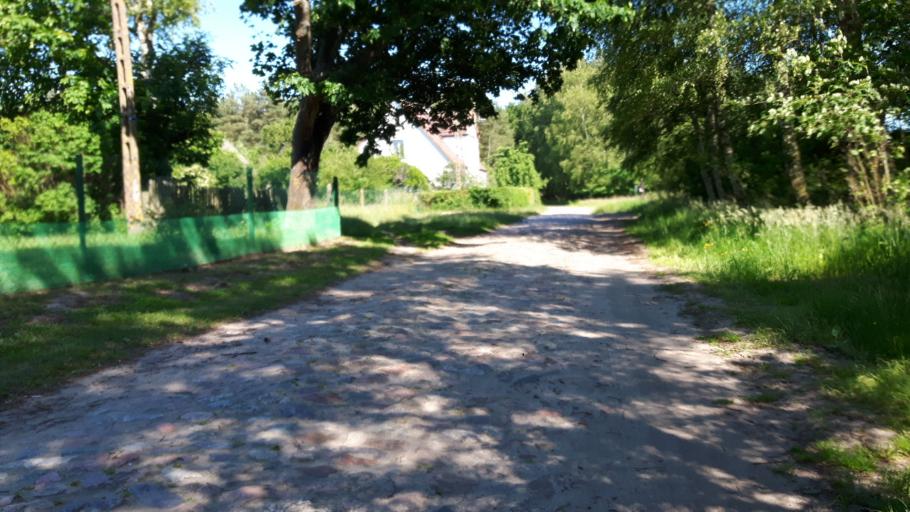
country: PL
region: Pomeranian Voivodeship
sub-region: Powiat leborski
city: Leba
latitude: 54.6941
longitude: 17.4613
